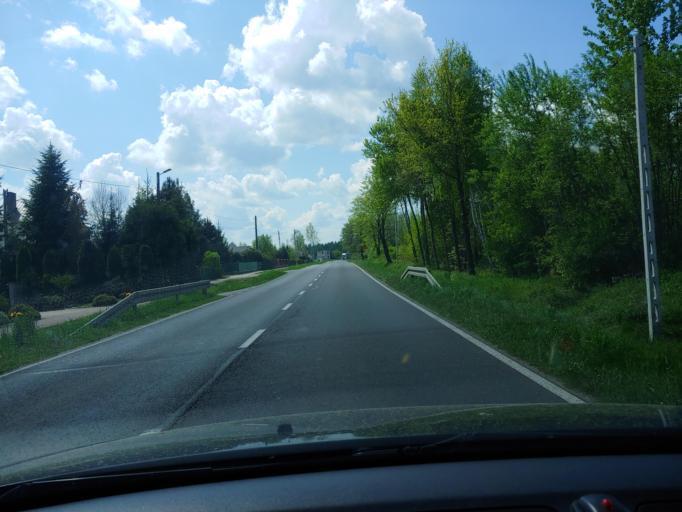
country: PL
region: Subcarpathian Voivodeship
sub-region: Powiat mielecki
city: Wadowice Gorne
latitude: 50.2415
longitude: 21.3008
